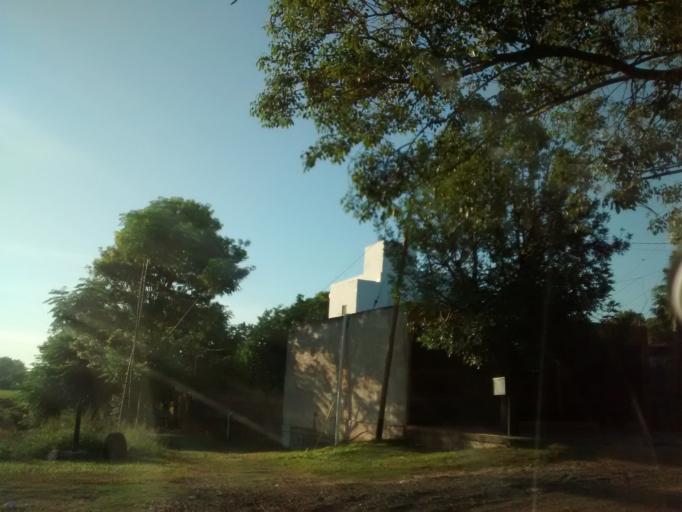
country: AR
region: Chaco
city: Resistencia
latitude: -27.4582
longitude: -58.9716
